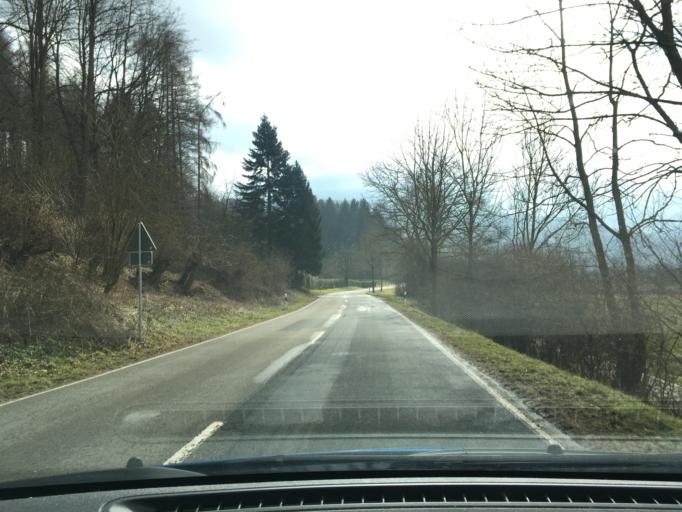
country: DE
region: Lower Saxony
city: Buhren
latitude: 51.5305
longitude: 9.6230
